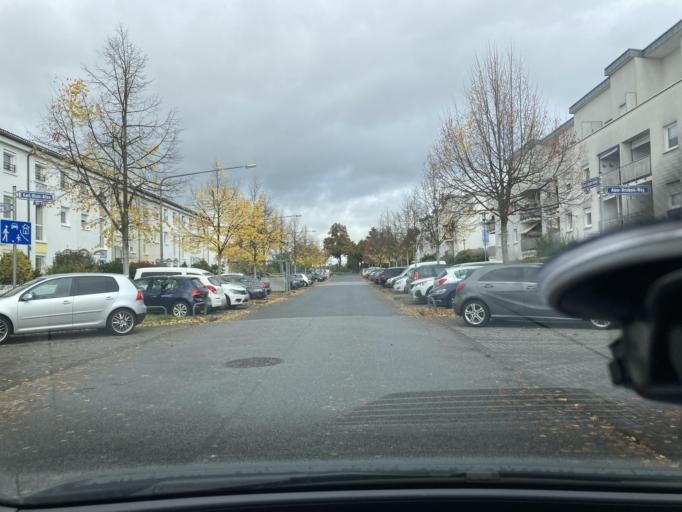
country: DE
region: Hesse
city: Sulzbach
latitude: 50.1137
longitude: 8.5515
